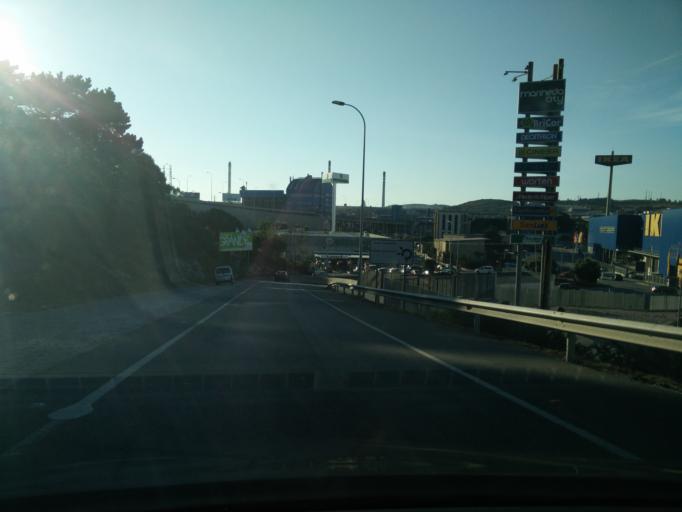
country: ES
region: Galicia
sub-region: Provincia da Coruna
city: A Coruna
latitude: 43.3423
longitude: -8.4298
